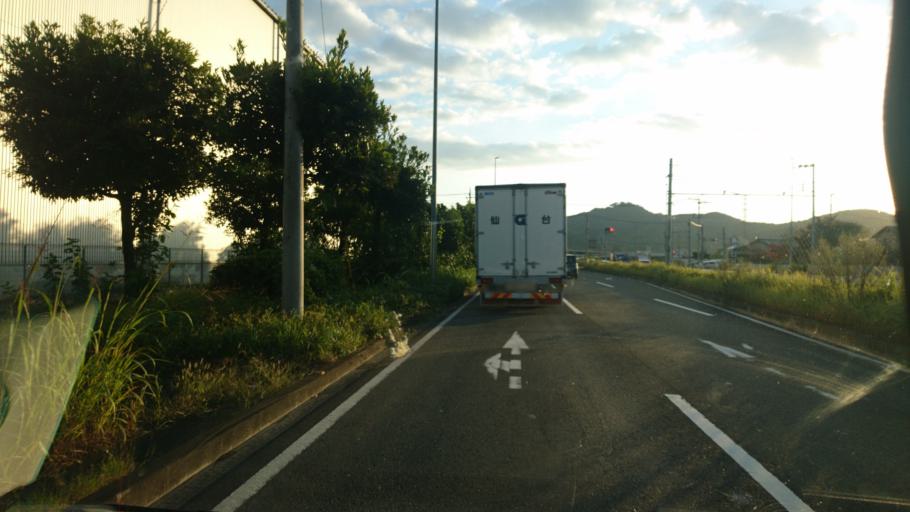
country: JP
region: Gunma
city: Ota
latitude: 36.3304
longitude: 139.3943
